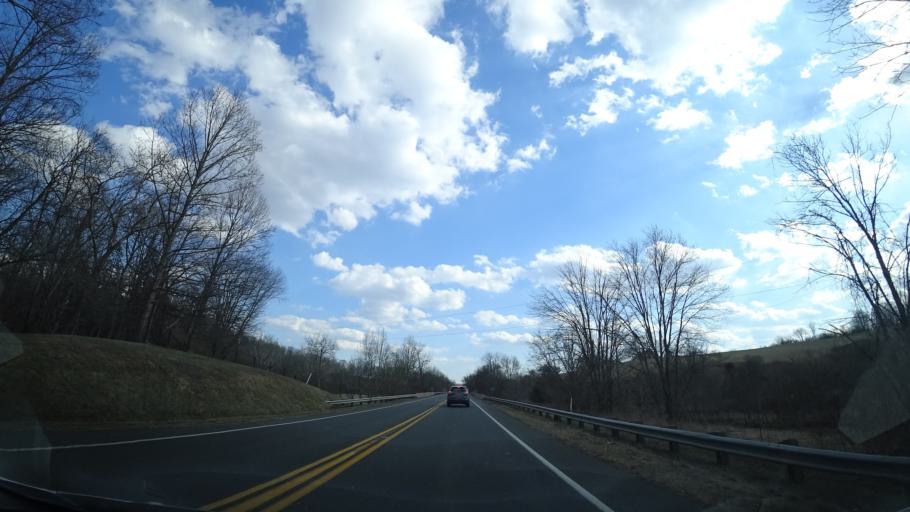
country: US
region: Virginia
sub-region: Fauquier County
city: Marshall
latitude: 38.9350
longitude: -77.9336
